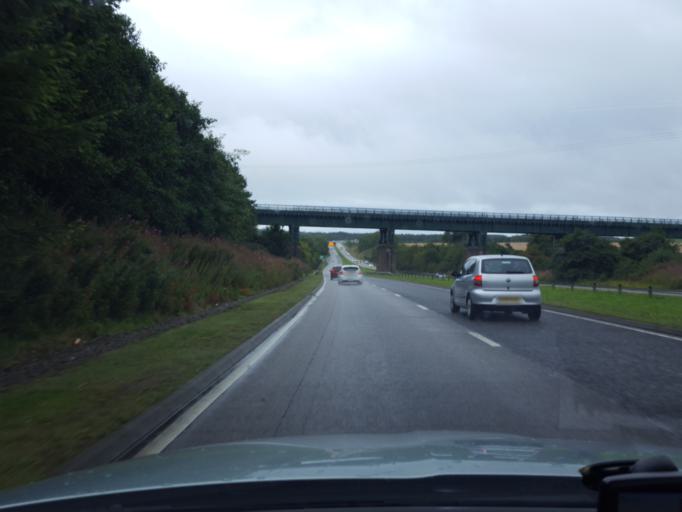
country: GB
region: Scotland
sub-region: Aberdeenshire
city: Stonehaven
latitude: 56.9633
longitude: -2.2391
